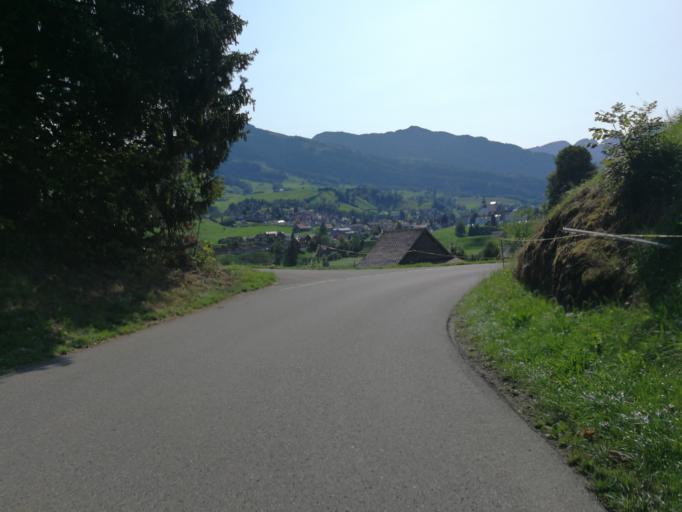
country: CH
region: Saint Gallen
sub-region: Wahlkreis Toggenburg
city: Krummenau
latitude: 47.2354
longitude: 9.1813
